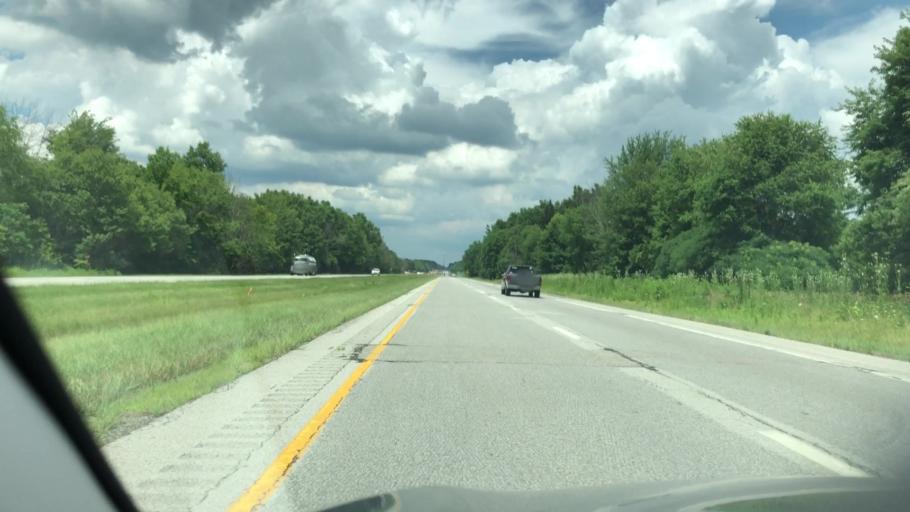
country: US
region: Ohio
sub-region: Summit County
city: Clinton
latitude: 40.9537
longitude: -81.6580
